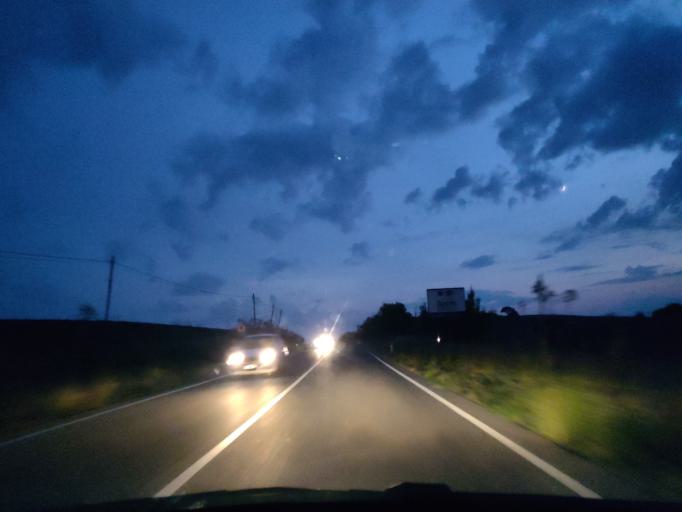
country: IT
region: Latium
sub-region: Provincia di Viterbo
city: Tarquinia
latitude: 42.2517
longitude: 11.8120
